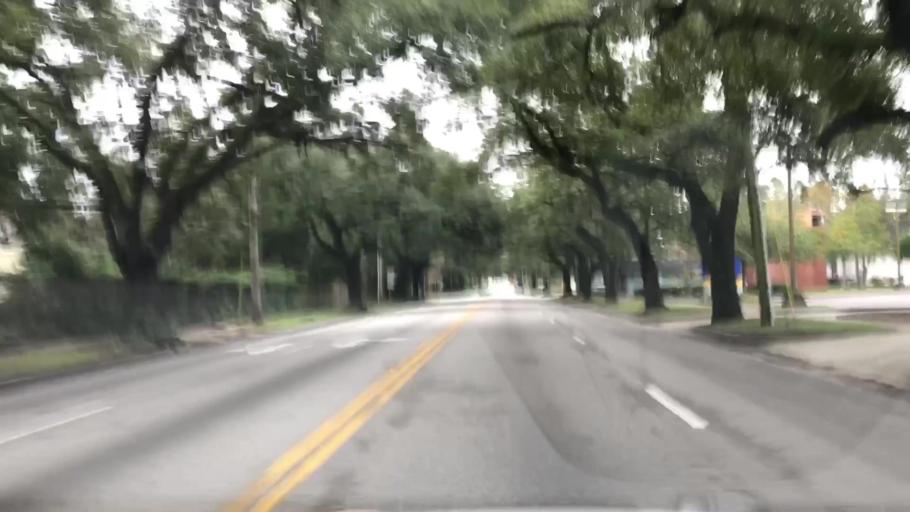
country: US
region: South Carolina
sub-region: Georgetown County
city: Georgetown
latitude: 33.3733
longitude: -79.2826
